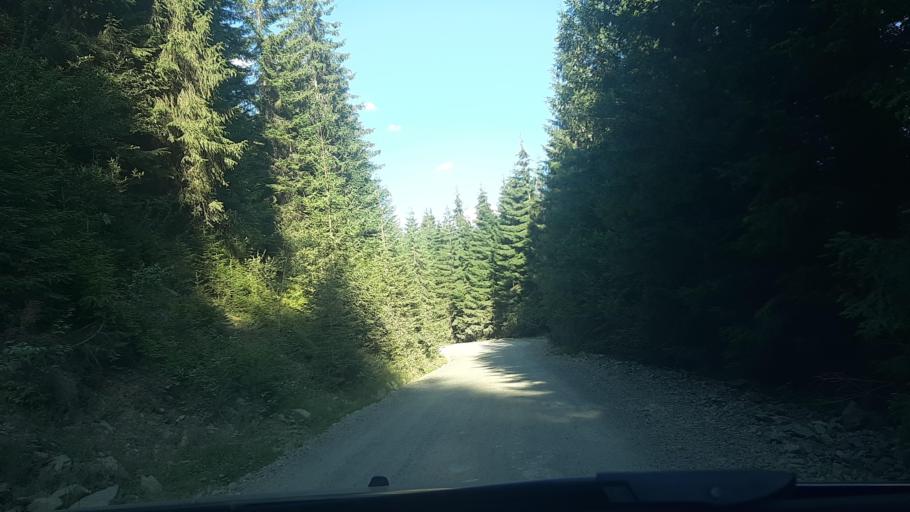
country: RO
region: Alba
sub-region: Comuna Sugag
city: Sugag
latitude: 45.5772
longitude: 23.6067
